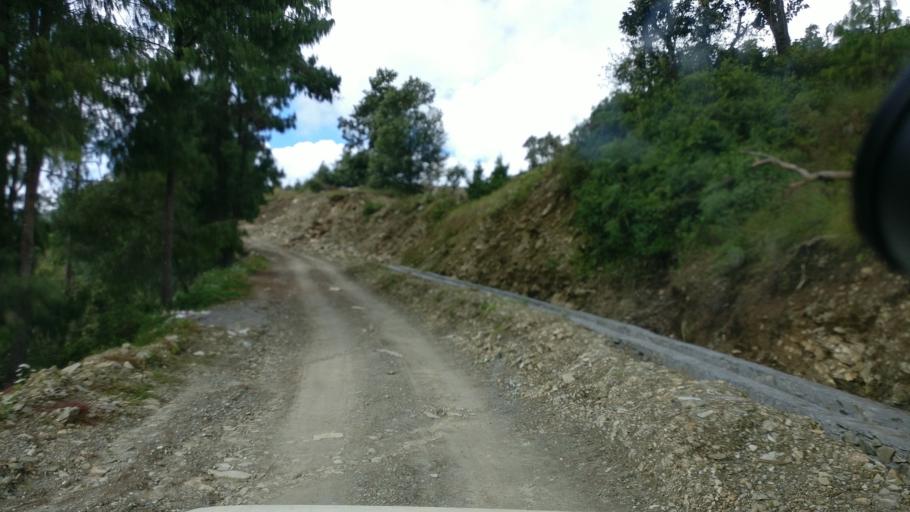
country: NP
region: Western Region
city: Baglung
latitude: 28.2837
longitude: 83.6393
